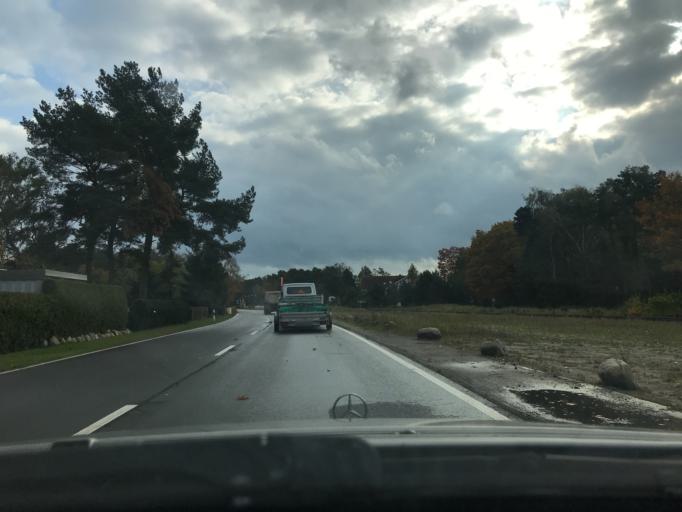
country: DE
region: Mecklenburg-Vorpommern
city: Karlshagen
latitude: 54.1196
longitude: 13.8283
